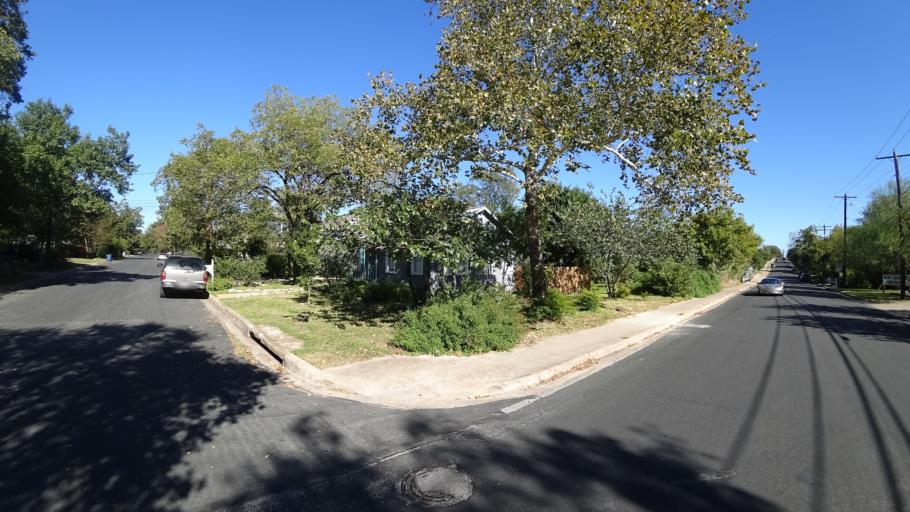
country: US
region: Texas
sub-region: Travis County
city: Austin
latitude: 30.3275
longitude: -97.7369
